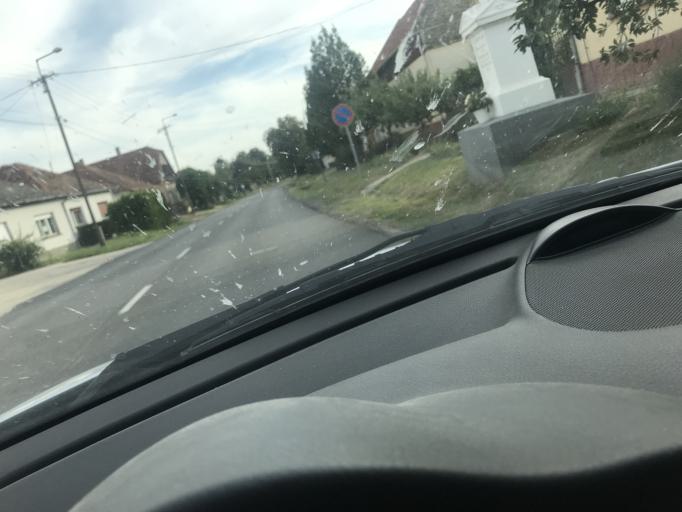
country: HU
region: Bacs-Kiskun
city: Csaszartoltes
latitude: 46.4285
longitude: 19.1816
